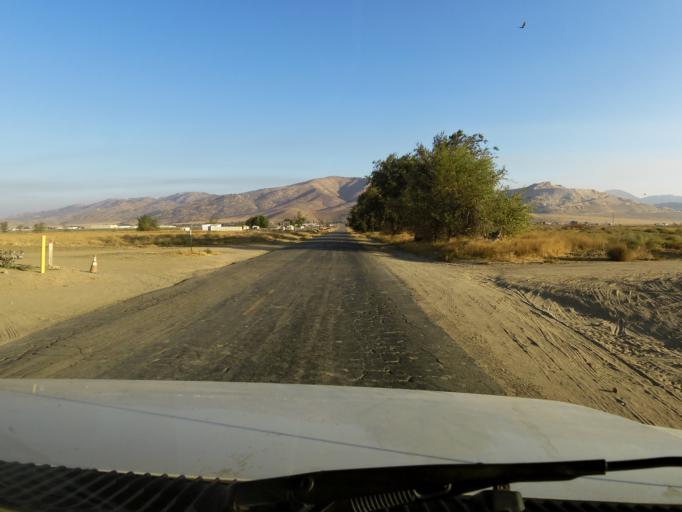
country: US
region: California
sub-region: Kern County
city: Tehachapi
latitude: 35.1132
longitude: -118.4145
